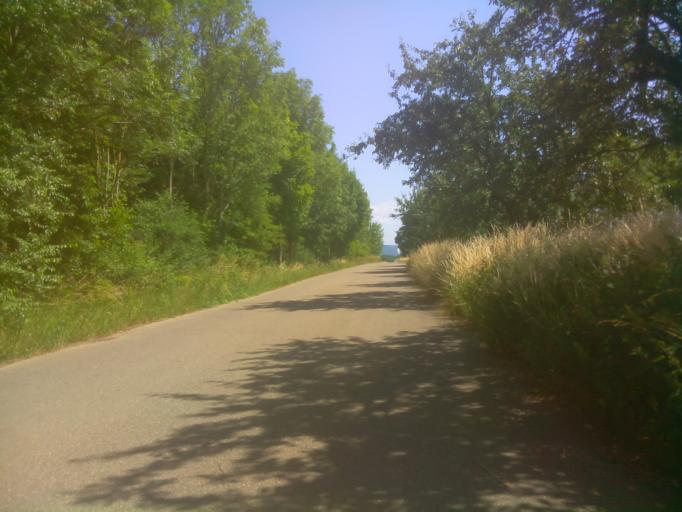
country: DE
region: Baden-Wuerttemberg
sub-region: Karlsruhe Region
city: Hemsbach
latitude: 49.5614
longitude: 8.6164
